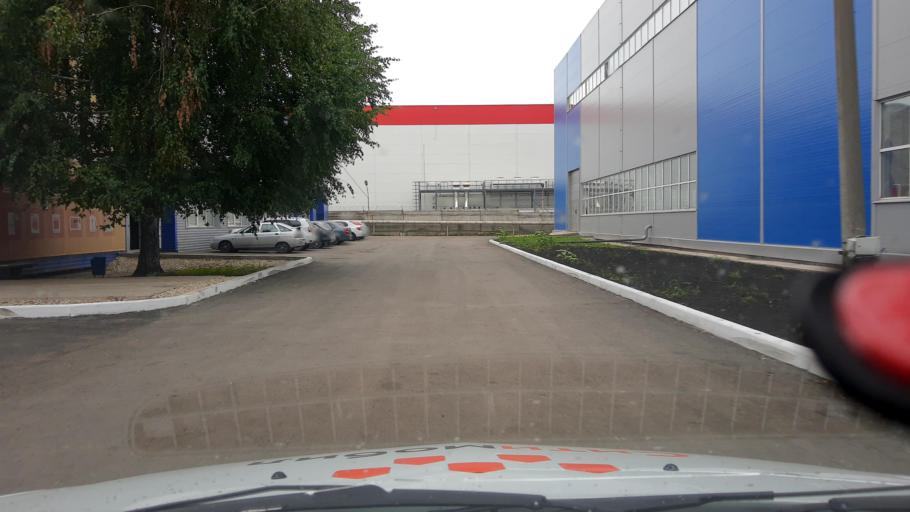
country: RU
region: Bashkortostan
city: Iglino
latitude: 54.7618
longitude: 56.2476
